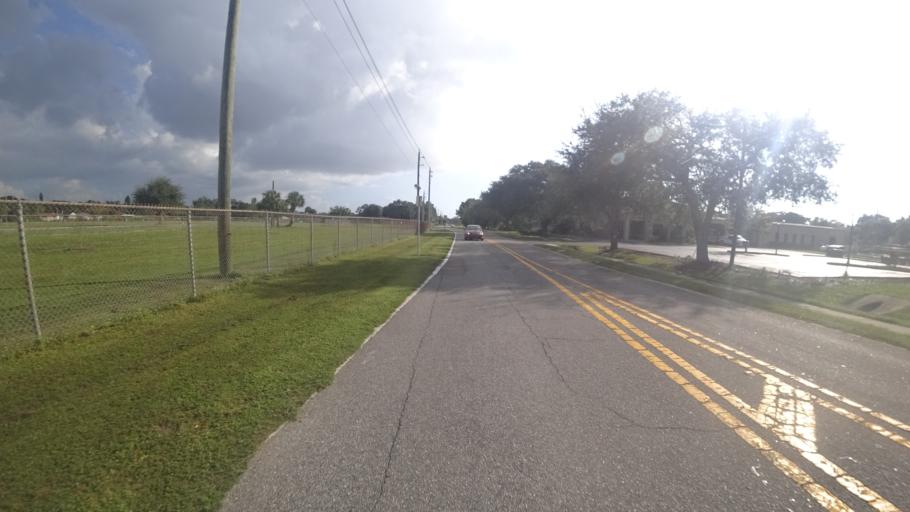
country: US
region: Florida
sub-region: Manatee County
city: Palmetto
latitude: 27.5249
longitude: -82.5812
